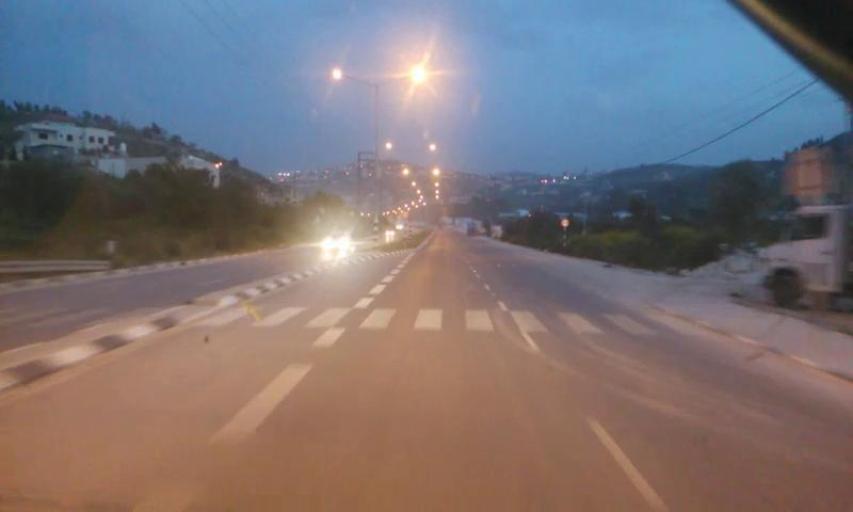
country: PS
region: West Bank
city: Dayr Sharaf
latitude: 32.2470
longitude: 35.1925
